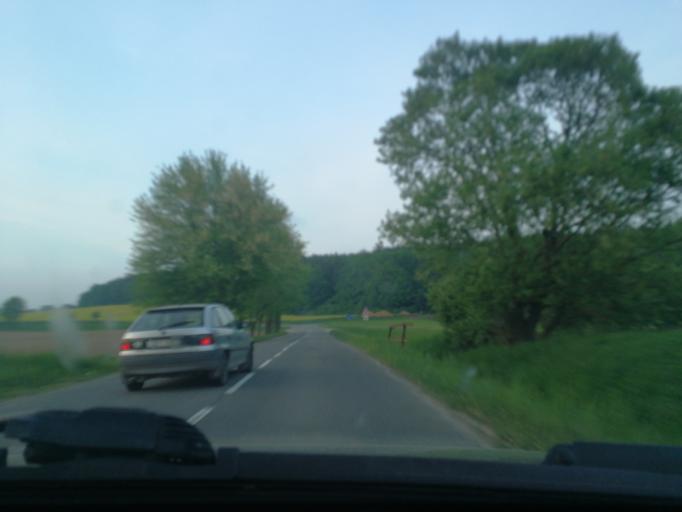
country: CZ
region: Zlin
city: Tecovice
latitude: 49.2492
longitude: 17.5705
